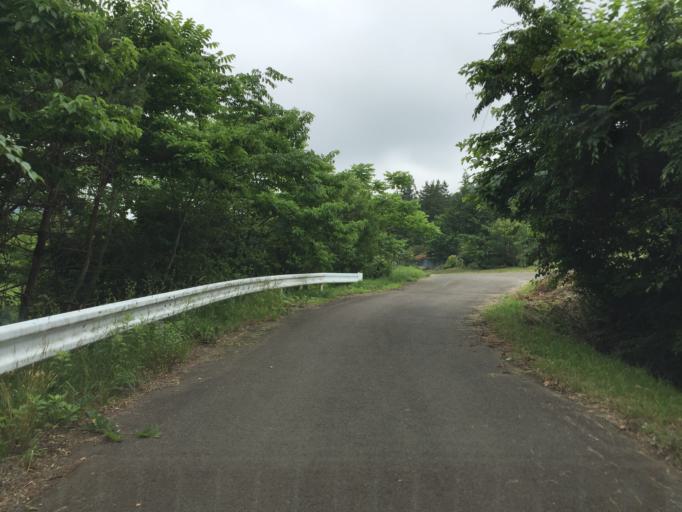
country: JP
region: Fukushima
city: Yanagawamachi-saiwaicho
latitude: 37.7855
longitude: 140.6909
